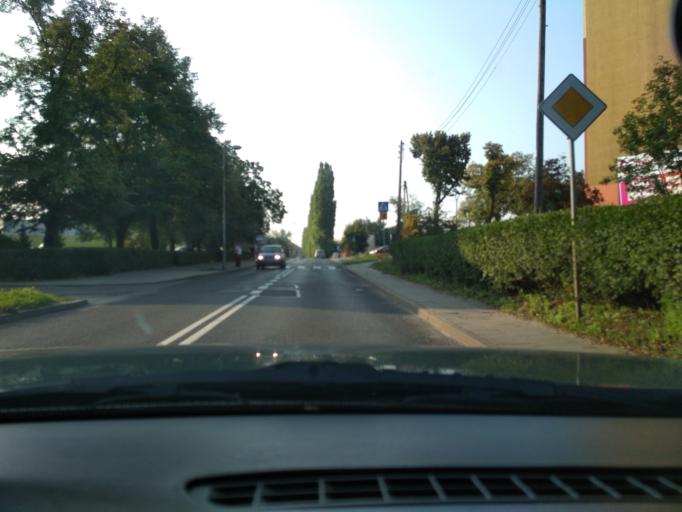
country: PL
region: Silesian Voivodeship
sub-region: Gliwice
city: Gliwice
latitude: 50.2833
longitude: 18.6756
